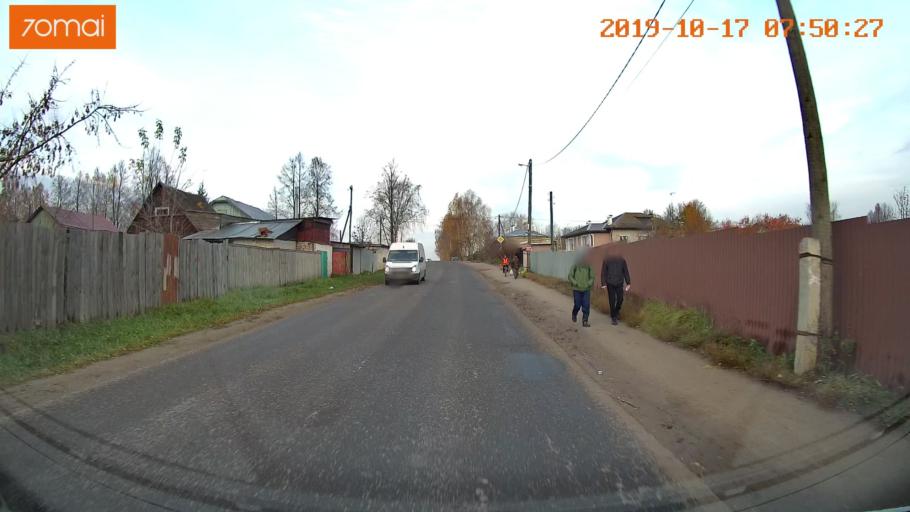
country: RU
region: Vladimir
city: Yur'yev-Pol'skiy
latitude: 56.4839
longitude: 39.6655
